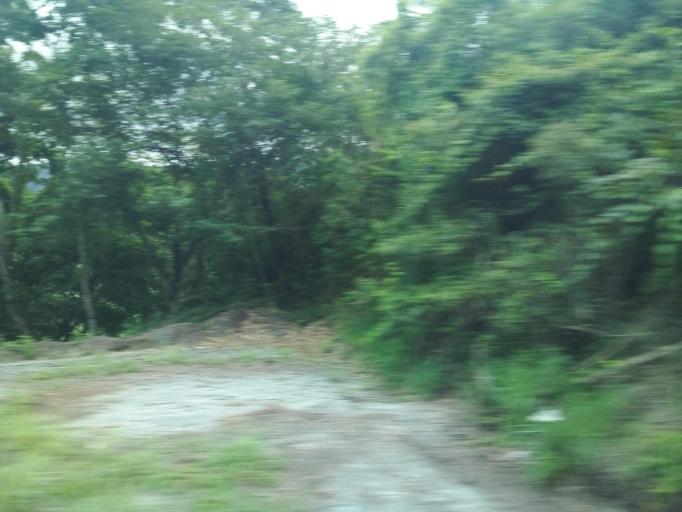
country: BR
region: Minas Gerais
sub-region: Nova Era
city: Nova Era
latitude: -19.6627
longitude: -42.8862
